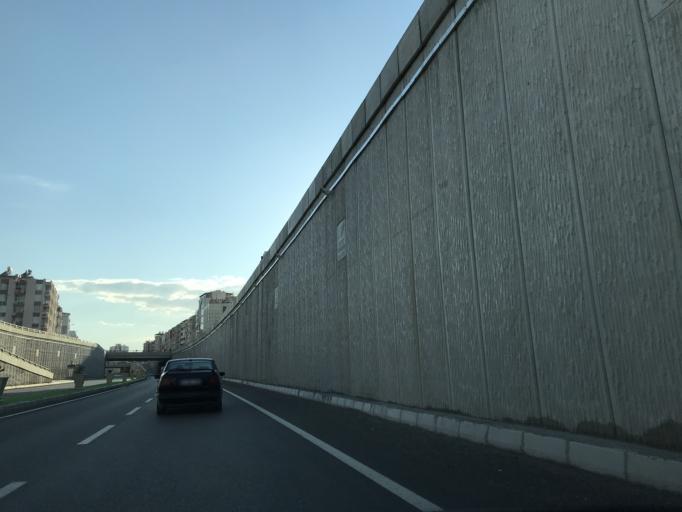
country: TR
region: Hatay
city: Iskenderun
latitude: 36.5847
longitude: 36.1742
